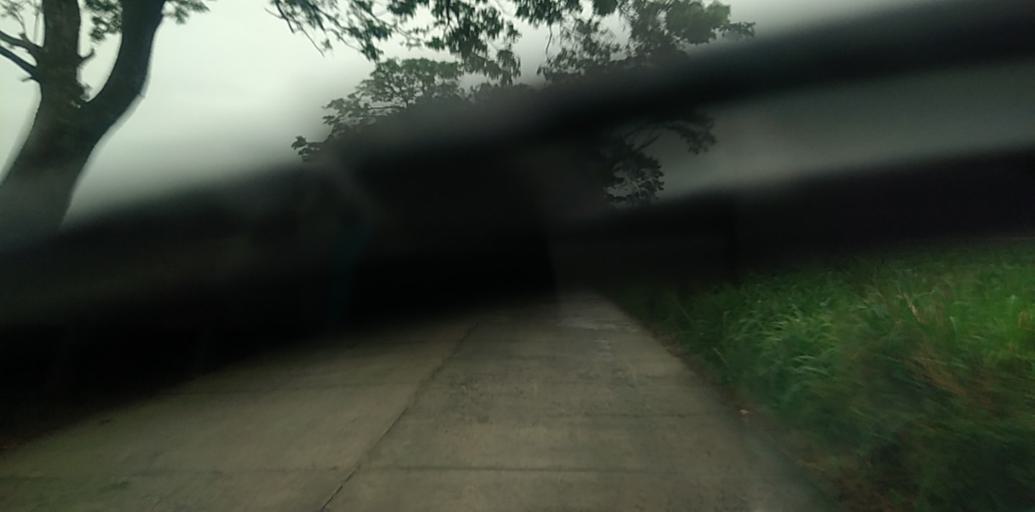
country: PH
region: Central Luzon
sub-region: Province of Pampanga
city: San Antonio
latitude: 15.1509
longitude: 120.7003
